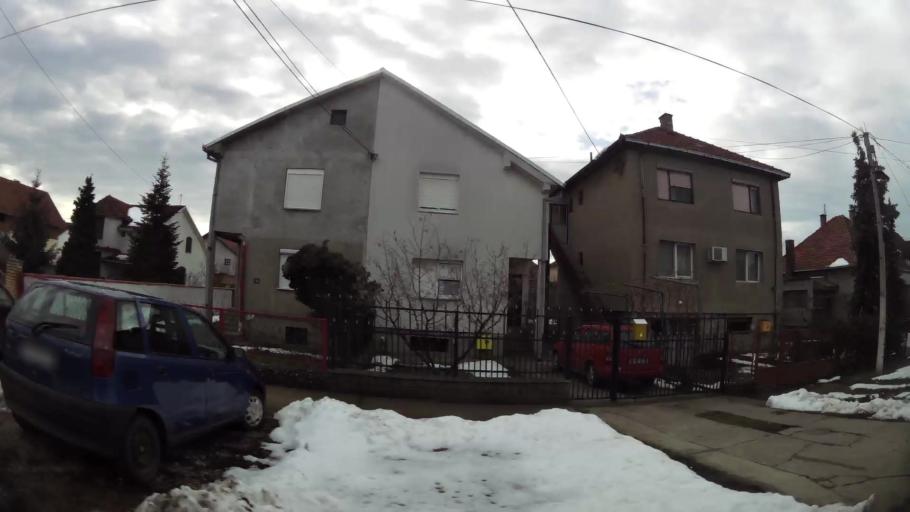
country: RS
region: Central Serbia
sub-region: Belgrade
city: Surcin
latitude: 44.8008
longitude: 20.2943
